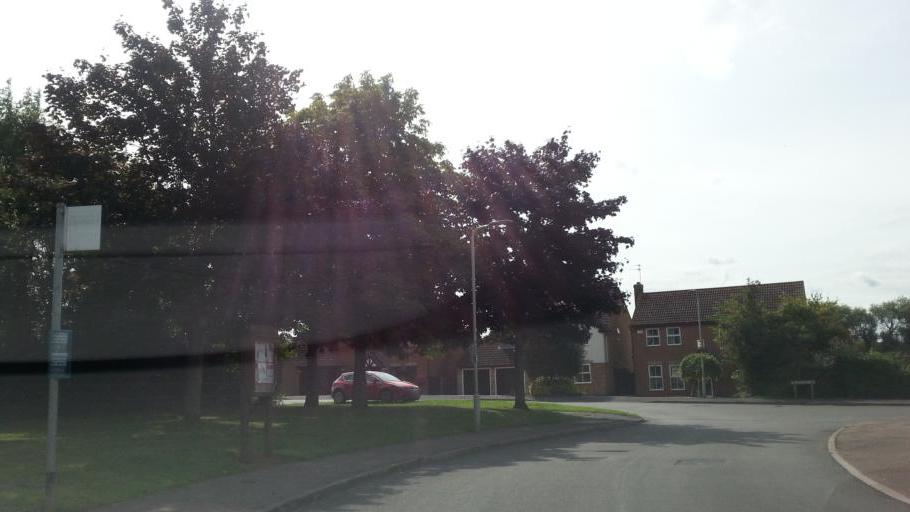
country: GB
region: England
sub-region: Leicestershire
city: Blaby
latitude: 52.5628
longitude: -1.1747
